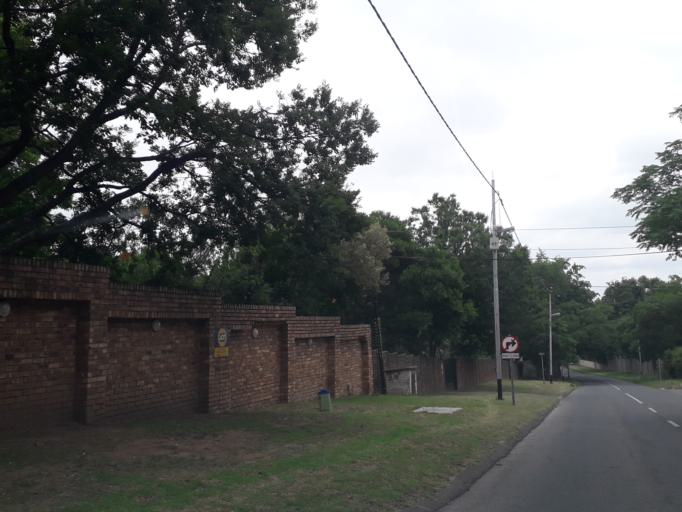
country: ZA
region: Gauteng
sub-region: City of Johannesburg Metropolitan Municipality
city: Midrand
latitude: -26.0490
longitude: 28.0387
